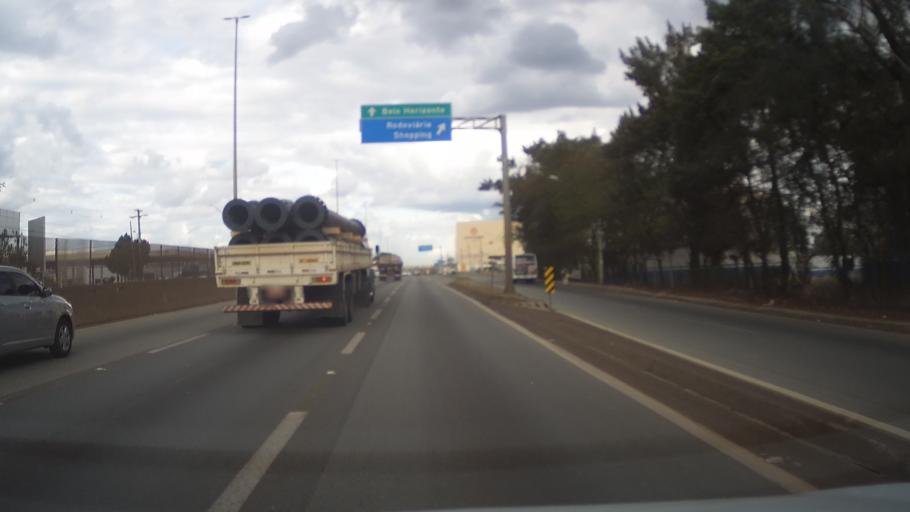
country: BR
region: Minas Gerais
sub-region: Betim
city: Betim
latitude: -19.9630
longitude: -44.1658
